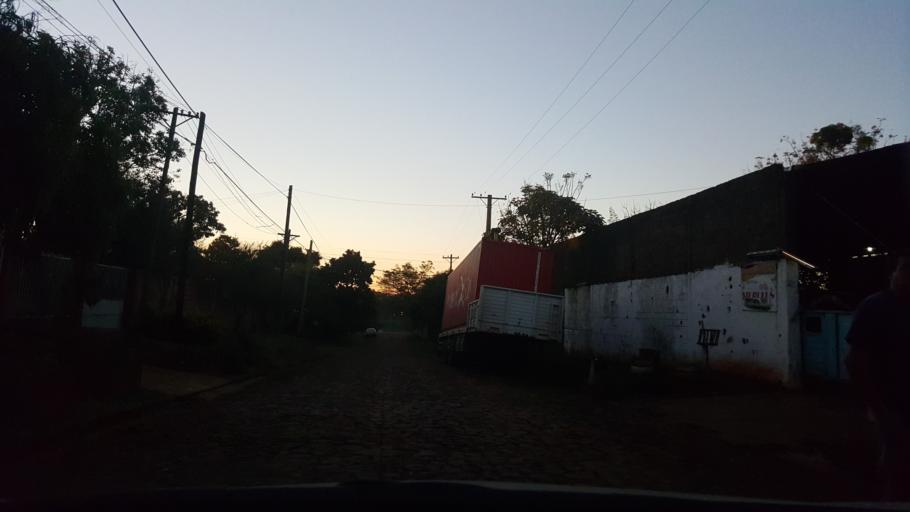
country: AR
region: Misiones
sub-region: Departamento de Capital
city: Posadas
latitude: -27.4234
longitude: -55.8997
